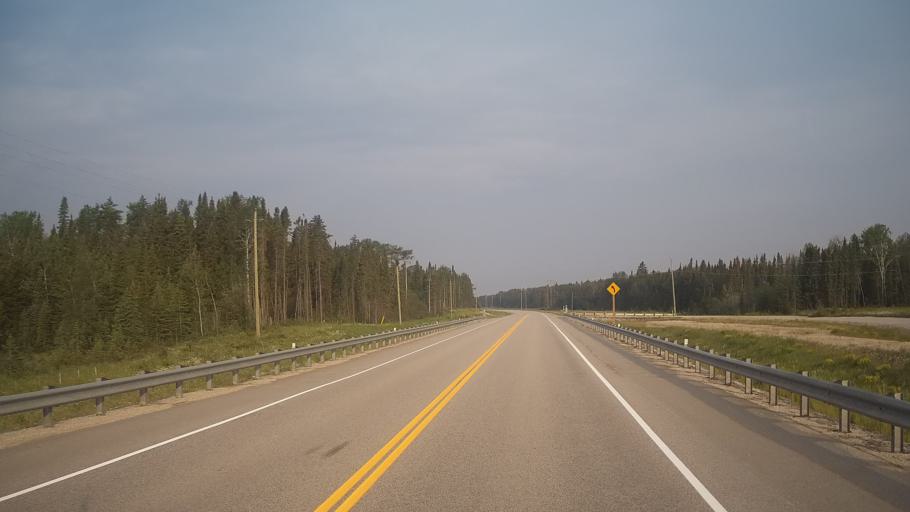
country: CA
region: Ontario
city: Hearst
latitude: 49.7395
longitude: -83.9616
